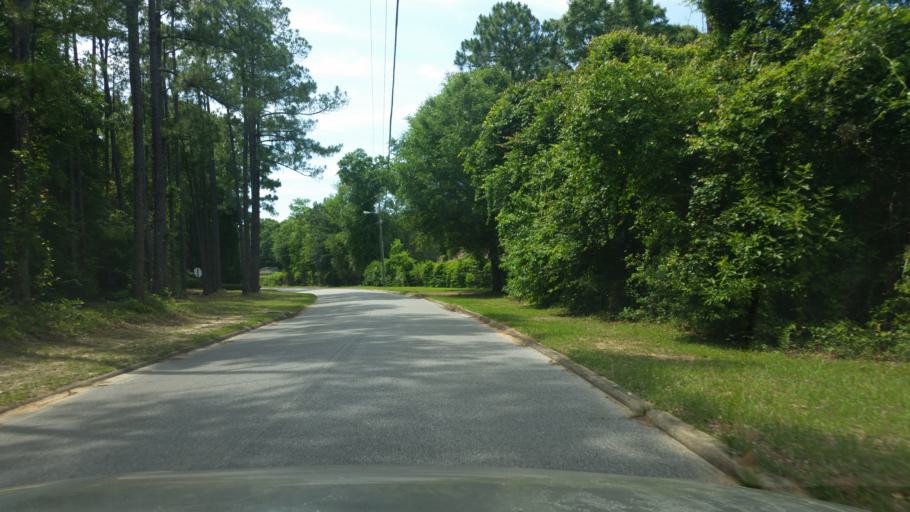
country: US
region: Florida
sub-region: Escambia County
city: Ferry Pass
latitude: 30.5299
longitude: -87.1908
